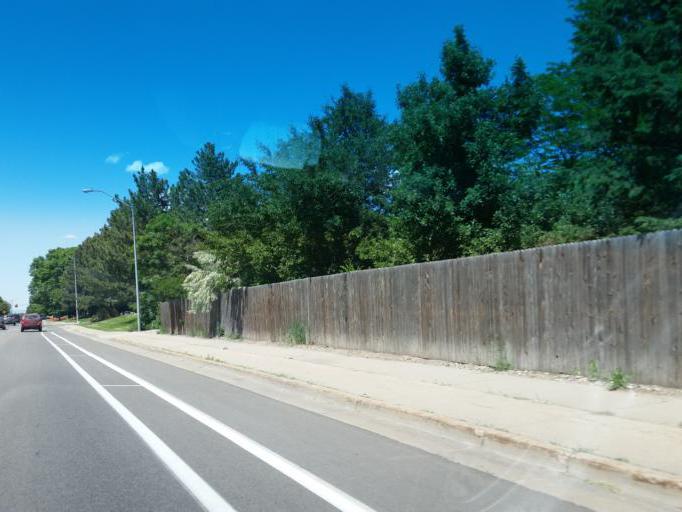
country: US
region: Colorado
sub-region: Larimer County
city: Fort Collins
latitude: 40.5499
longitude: -105.0960
